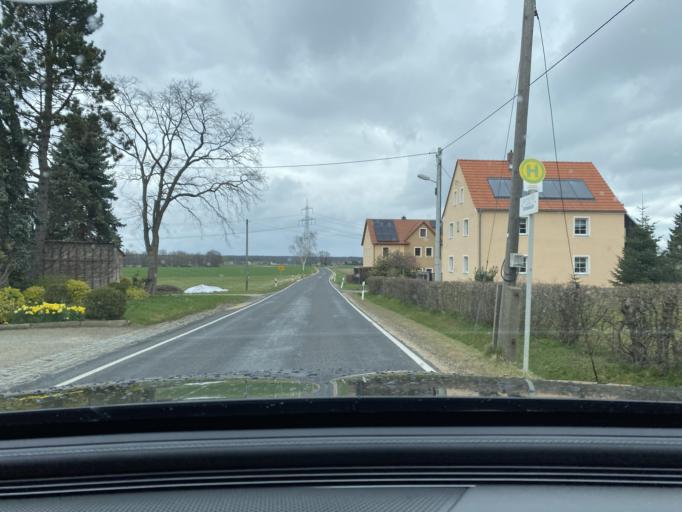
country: DE
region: Saxony
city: Radibor
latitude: 51.2617
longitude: 14.4281
